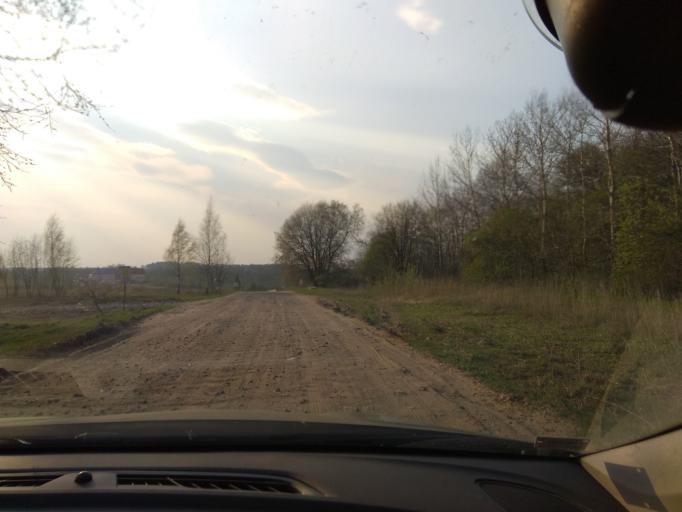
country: LT
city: Baltoji Voke
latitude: 54.5941
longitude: 25.1674
